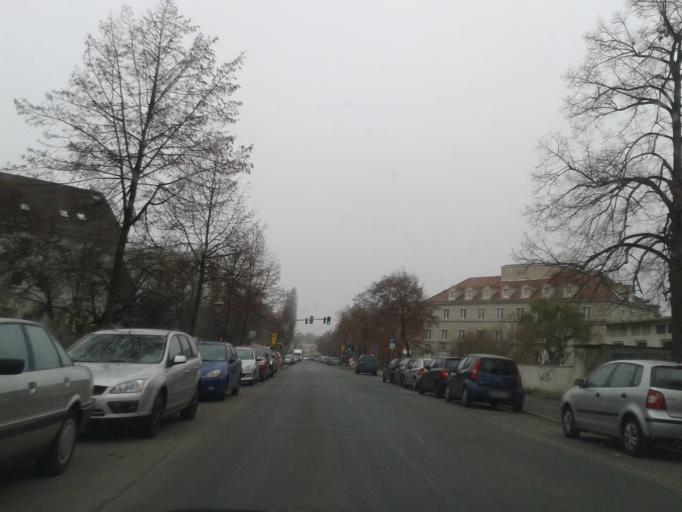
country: DE
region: Saxony
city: Dresden
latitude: 51.0894
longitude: 13.7102
